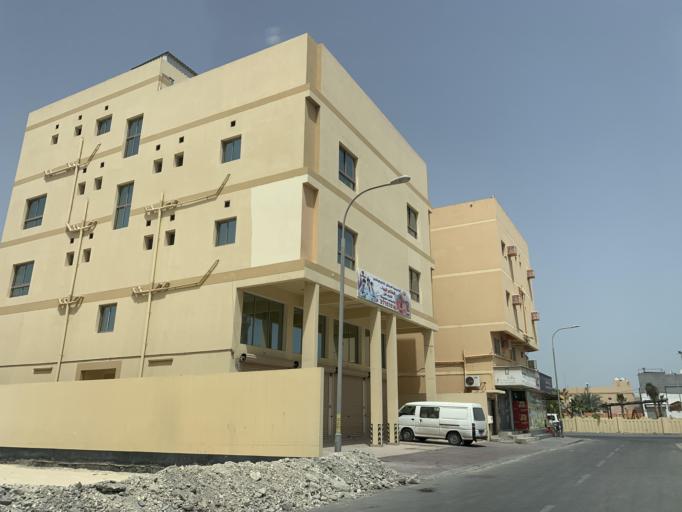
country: BH
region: Northern
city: Sitrah
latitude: 26.1407
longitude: 50.6018
